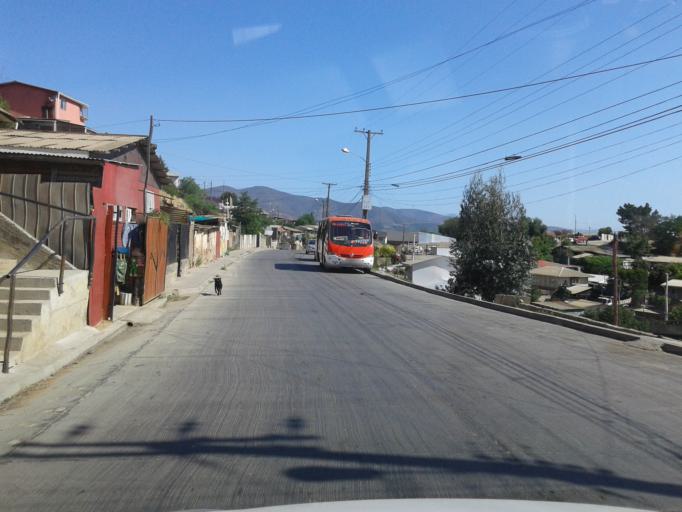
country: CL
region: Valparaiso
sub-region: Provincia de Quillota
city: Quillota
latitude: -32.8735
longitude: -71.2527
